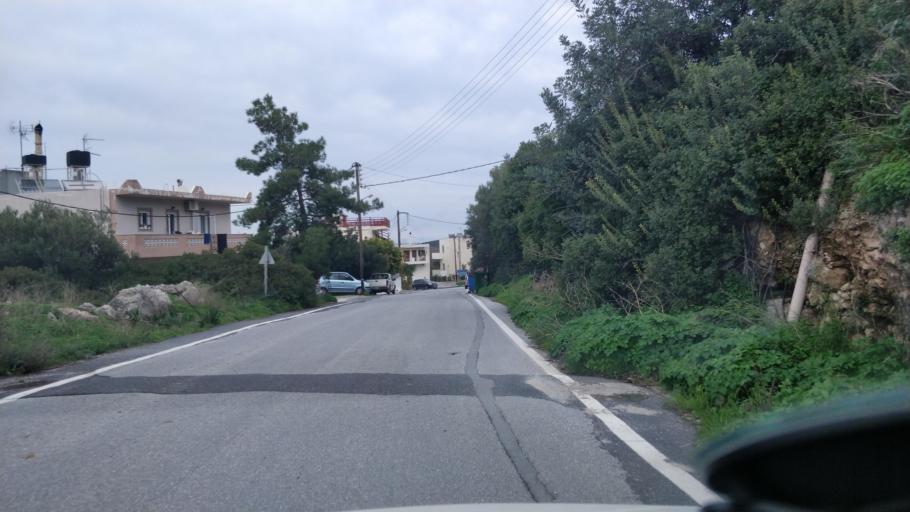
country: GR
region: Crete
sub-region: Nomos Lasithiou
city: Agios Nikolaos
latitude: 35.1201
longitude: 25.7268
